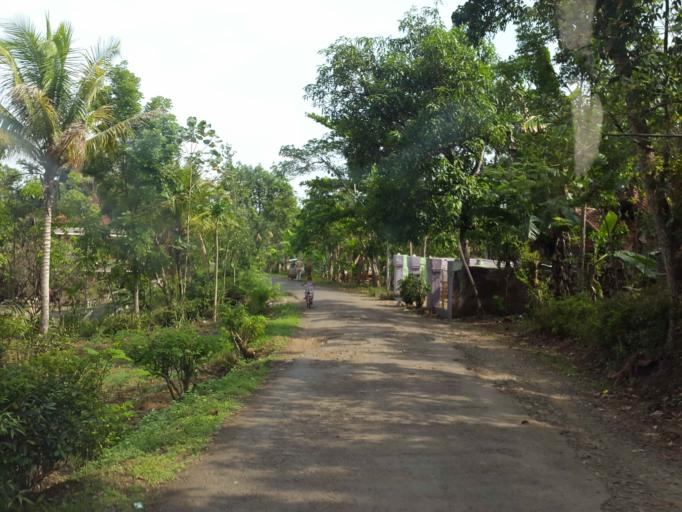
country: ID
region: Central Java
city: Sogati
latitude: -7.3253
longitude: 108.6757
